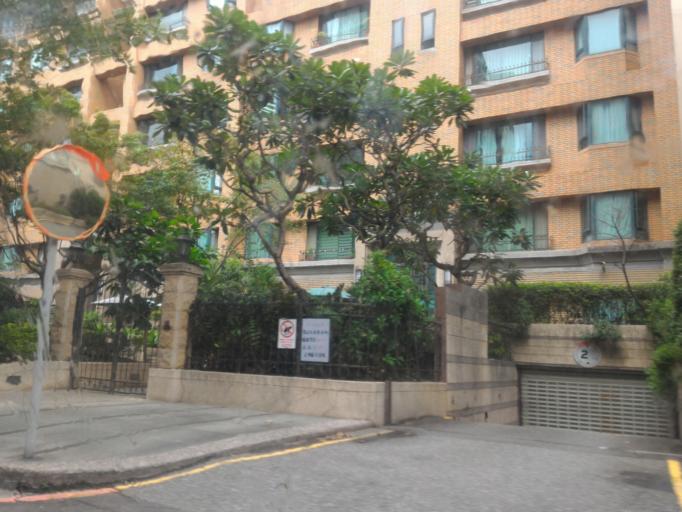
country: TW
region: Taipei
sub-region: Taipei
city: Banqiao
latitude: 25.0872
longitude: 121.4587
